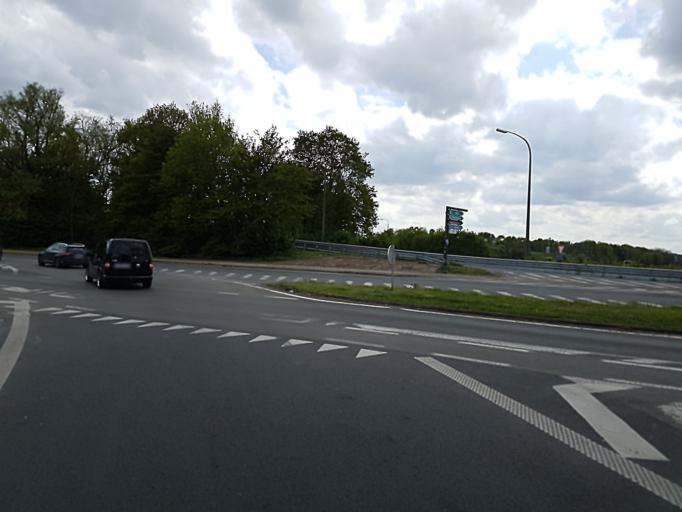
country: BE
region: Wallonia
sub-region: Province du Hainaut
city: Tournai
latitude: 50.6296
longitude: 3.3601
